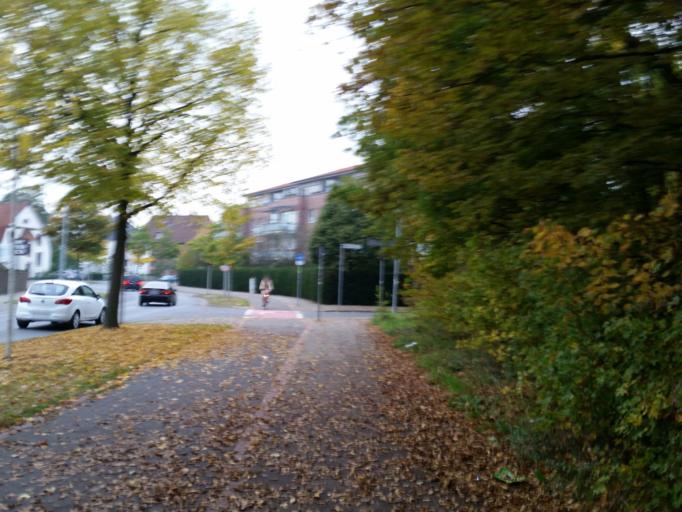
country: DE
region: Lower Saxony
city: Laatzen
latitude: 52.3394
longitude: 9.8303
